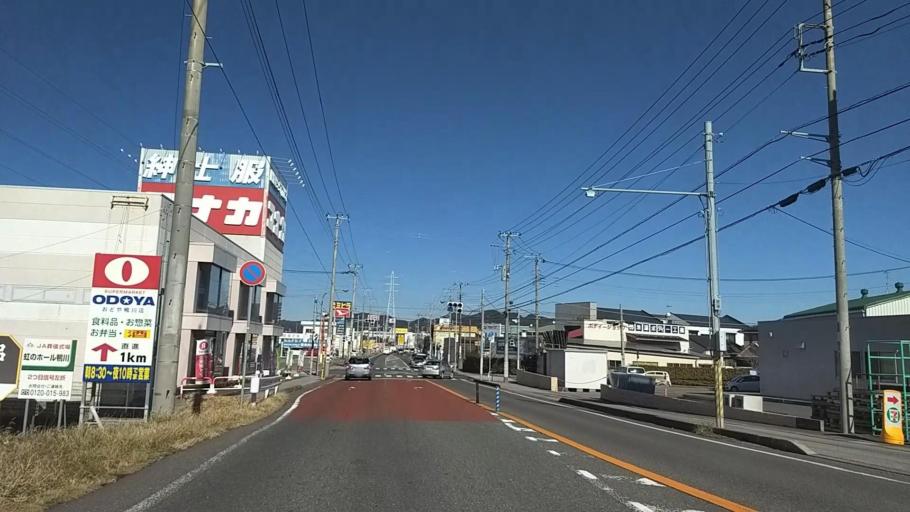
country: JP
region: Chiba
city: Kawaguchi
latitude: 35.0997
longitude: 140.0937
